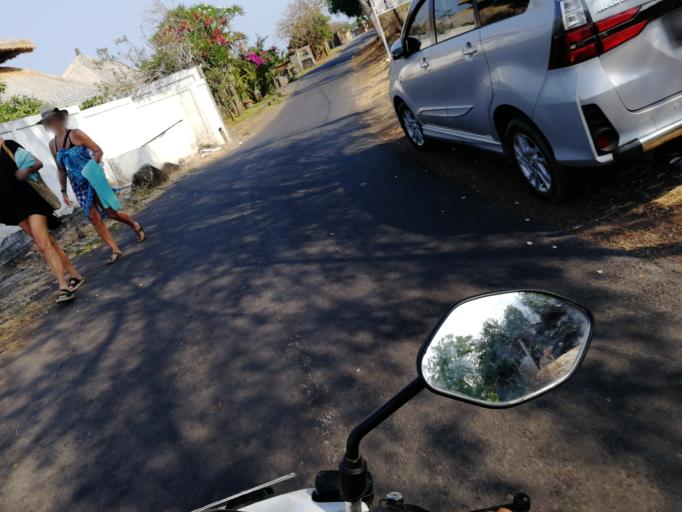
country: ID
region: Bali
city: Biaslantang Kaler
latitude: -8.3588
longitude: 115.6974
